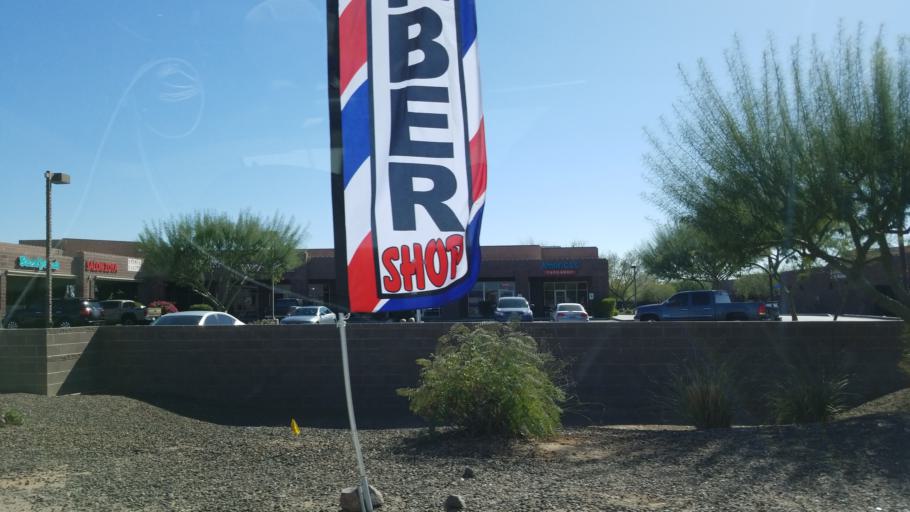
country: US
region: Arizona
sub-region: Maricopa County
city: Scottsdale
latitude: 33.5534
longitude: -111.8817
